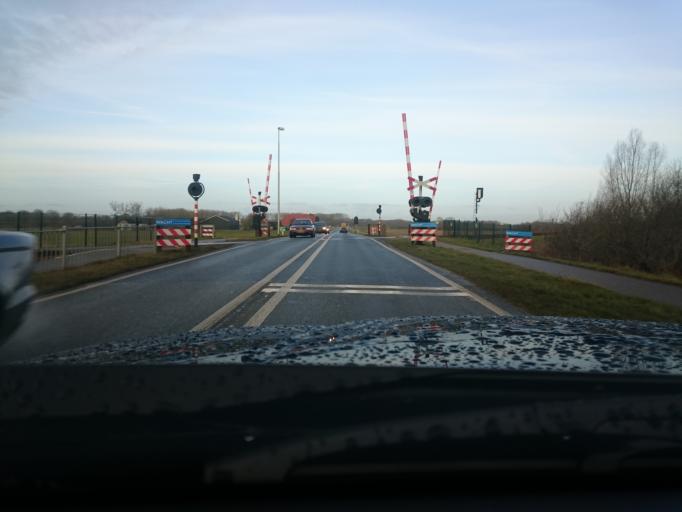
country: NL
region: Gelderland
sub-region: Gemeente Voorst
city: Voorst
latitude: 52.1471
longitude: 6.1626
